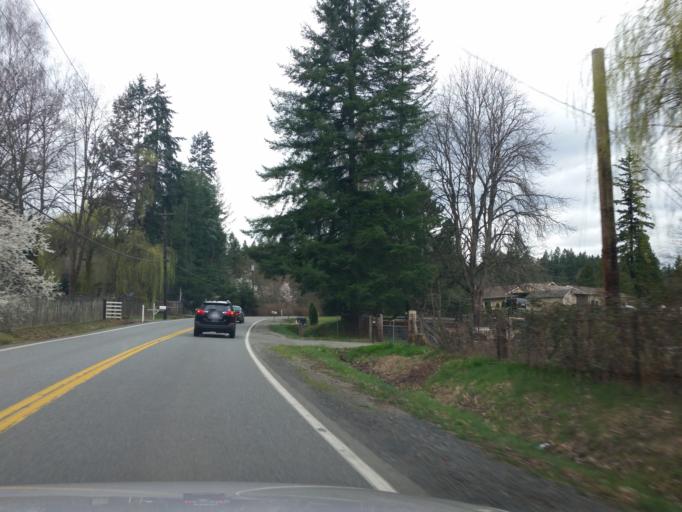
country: US
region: Washington
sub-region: Snohomish County
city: North Creek
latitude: 47.8055
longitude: -122.1608
